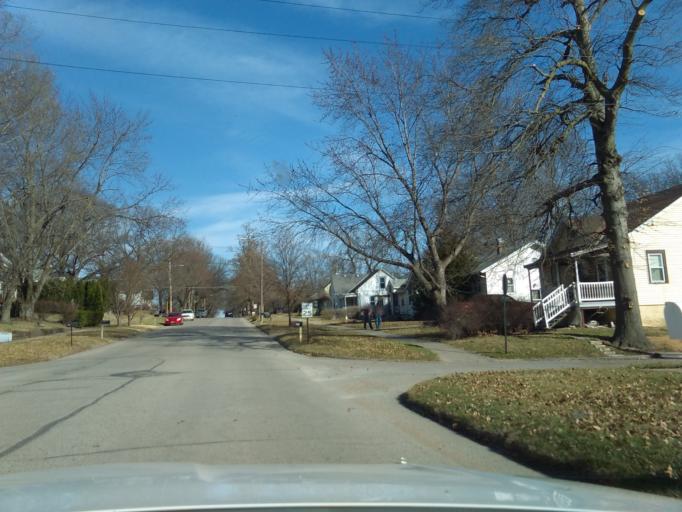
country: US
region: Nebraska
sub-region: Otoe County
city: Nebraska City
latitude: 40.6768
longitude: -95.8716
